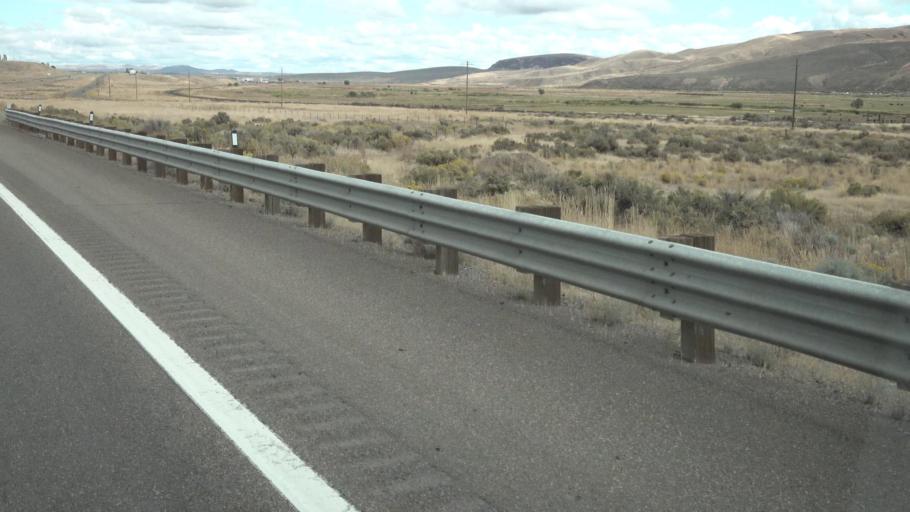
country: US
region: Nevada
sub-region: Elko County
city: Elko
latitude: 40.9142
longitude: -115.6920
